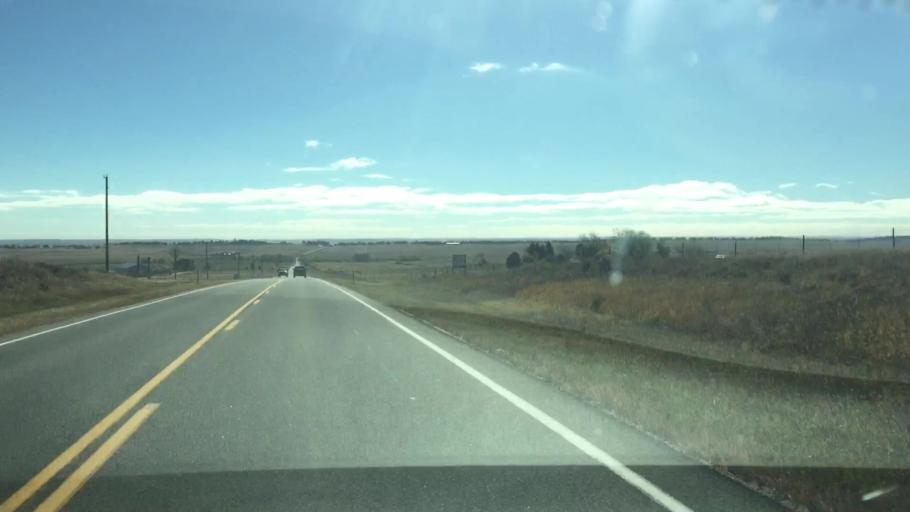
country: US
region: Colorado
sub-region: Elbert County
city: Kiowa
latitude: 39.3292
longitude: -104.4056
